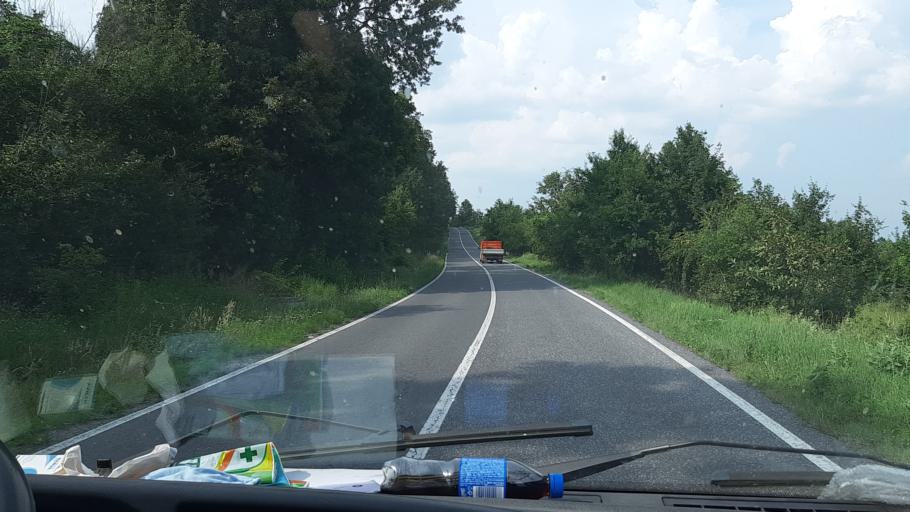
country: RO
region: Caras-Severin
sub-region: Comuna Farliug
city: Farliug
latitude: 45.5379
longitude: 21.8762
